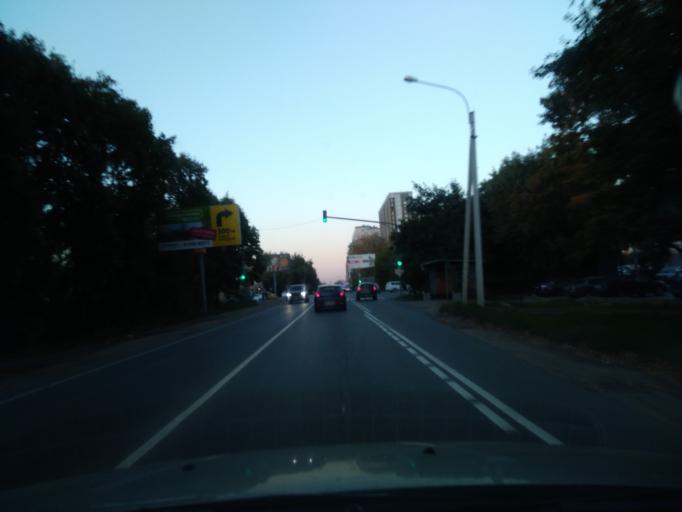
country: RU
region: Moscow
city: Strogino
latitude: 55.8642
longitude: 37.3905
